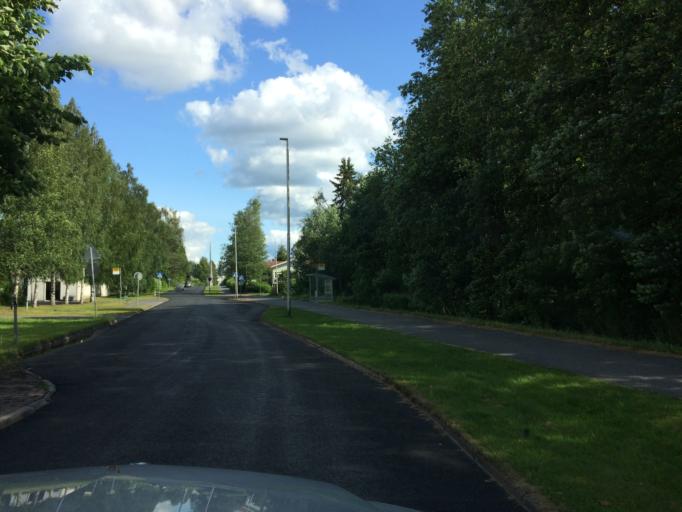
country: FI
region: Haeme
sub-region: Haemeenlinna
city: Haemeenlinna
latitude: 60.9854
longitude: 24.3982
